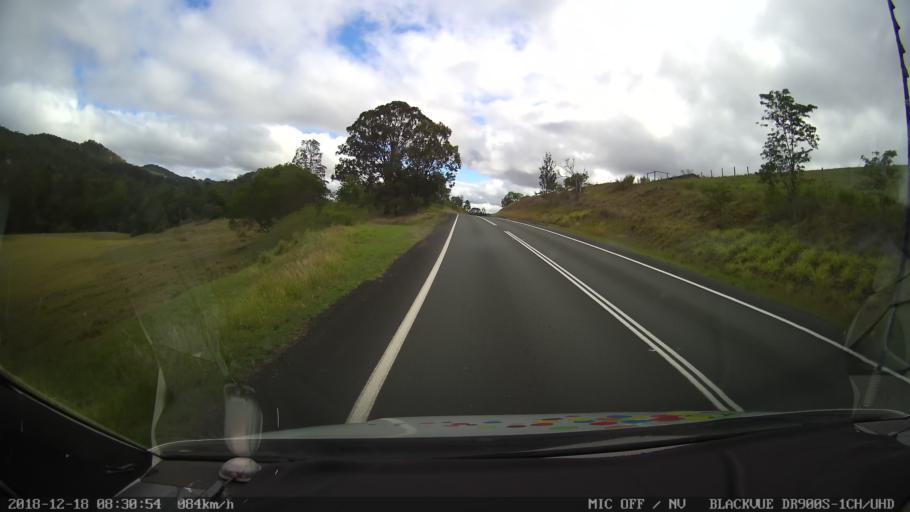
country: AU
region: New South Wales
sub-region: Kyogle
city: Kyogle
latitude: -28.3183
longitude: 152.7735
